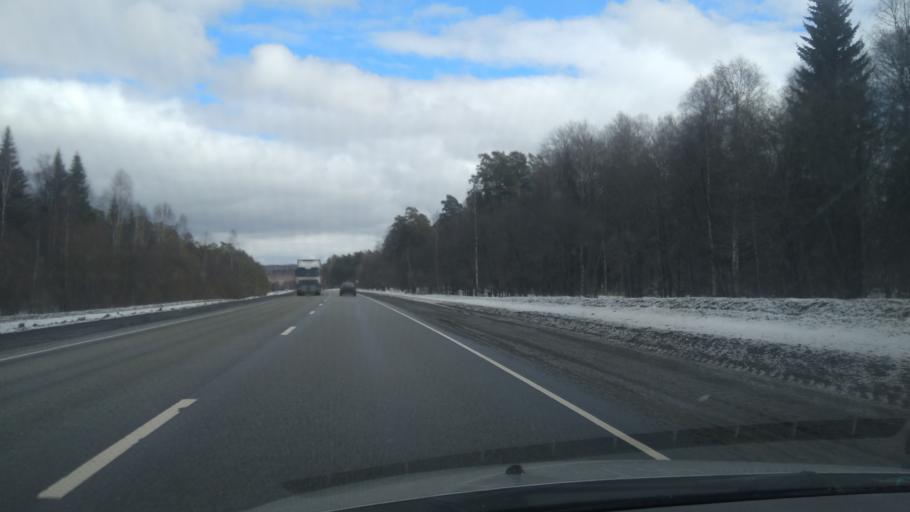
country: RU
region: Sverdlovsk
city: Bisert'
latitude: 56.8320
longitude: 58.8190
